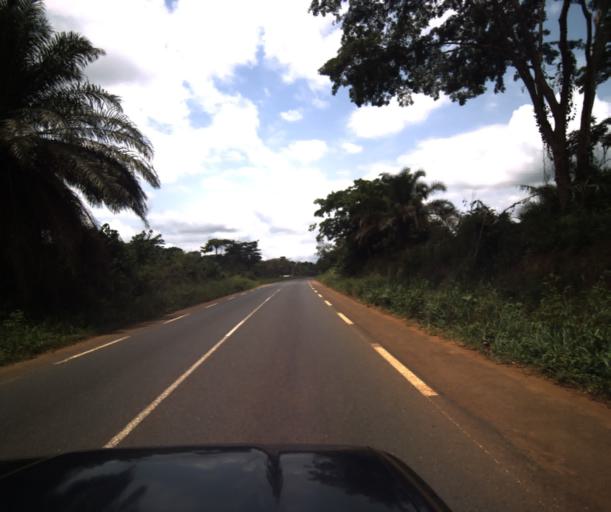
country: CM
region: Centre
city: Eseka
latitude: 3.8719
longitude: 10.8978
